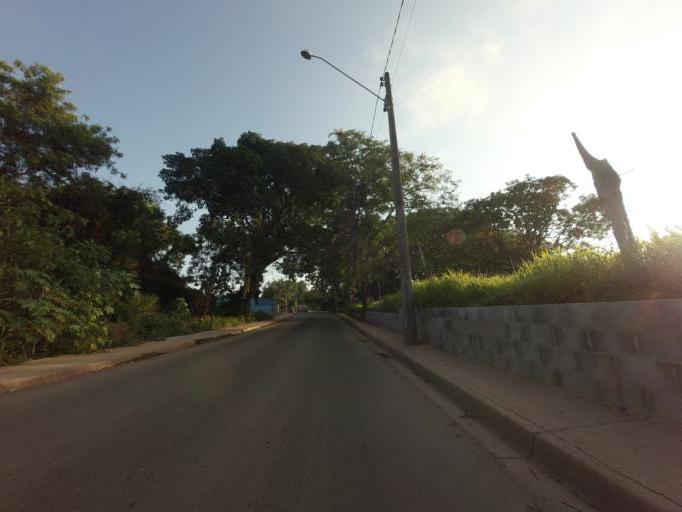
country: BR
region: Sao Paulo
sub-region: Piracicaba
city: Piracicaba
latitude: -22.7502
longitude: -47.6109
